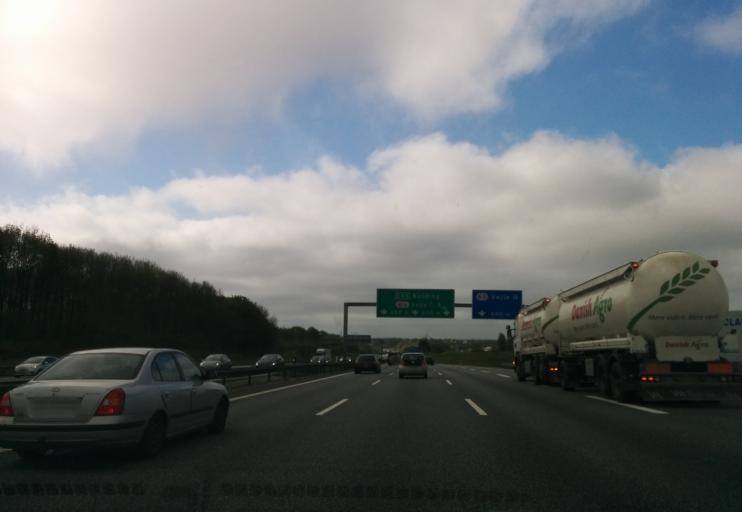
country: DK
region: South Denmark
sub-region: Vejle Kommune
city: Vejle
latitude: 55.7340
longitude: 9.5765
